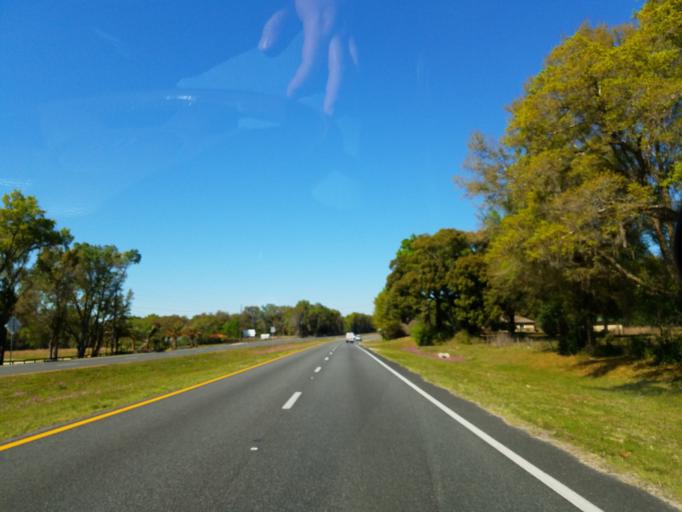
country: US
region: Florida
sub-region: Marion County
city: Belleview
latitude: 29.0190
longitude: -82.0448
